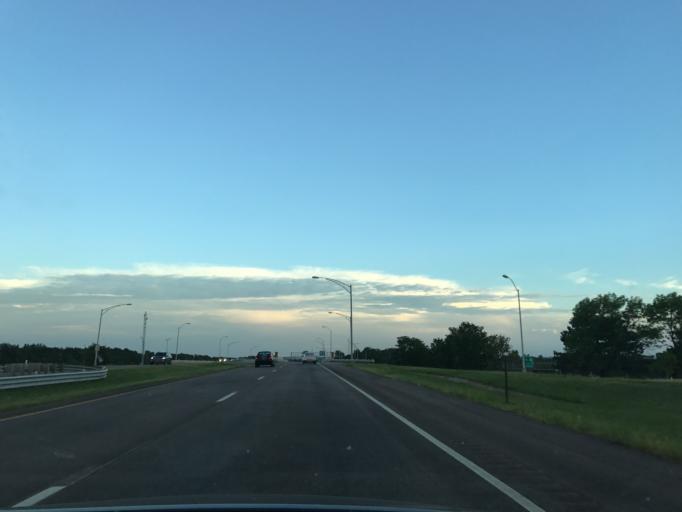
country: US
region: Nebraska
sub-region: Lancaster County
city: Lincoln
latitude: 40.8641
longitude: -96.7168
